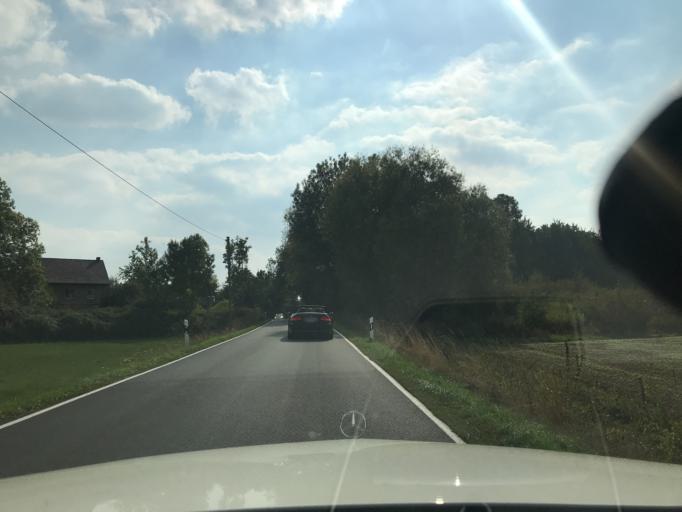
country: DE
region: North Rhine-Westphalia
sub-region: Regierungsbezirk Arnsberg
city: Werl
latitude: 51.5968
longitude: 7.8748
